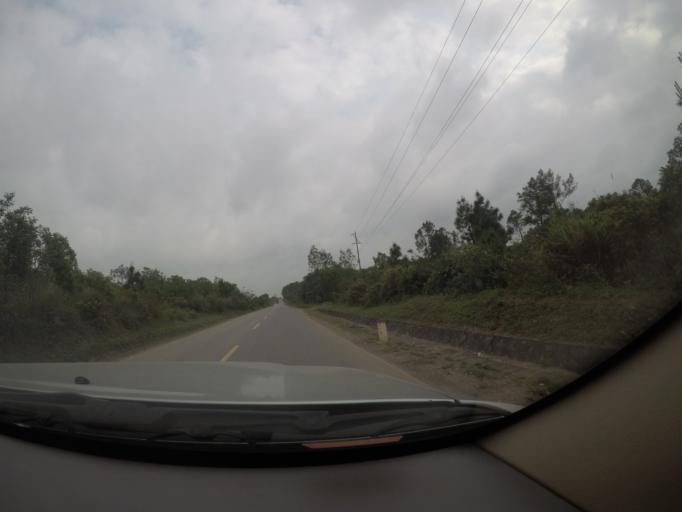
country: VN
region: Quang Binh
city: Quan Hau
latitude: 17.4004
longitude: 106.6074
